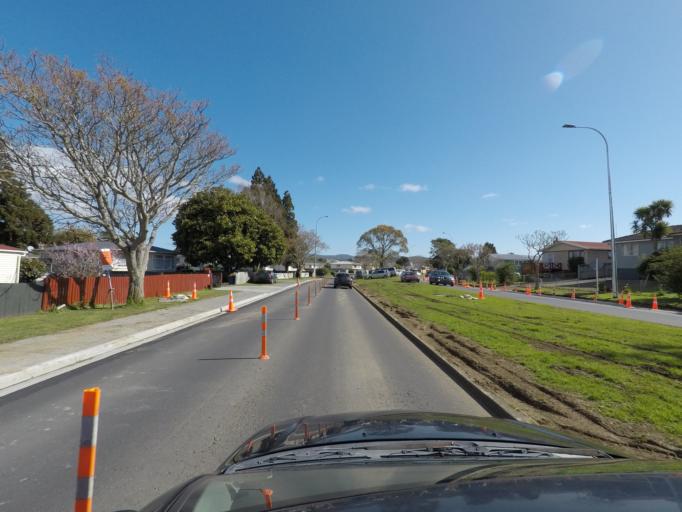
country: NZ
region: Auckland
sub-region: Auckland
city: Rosebank
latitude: -36.8567
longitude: 174.6198
